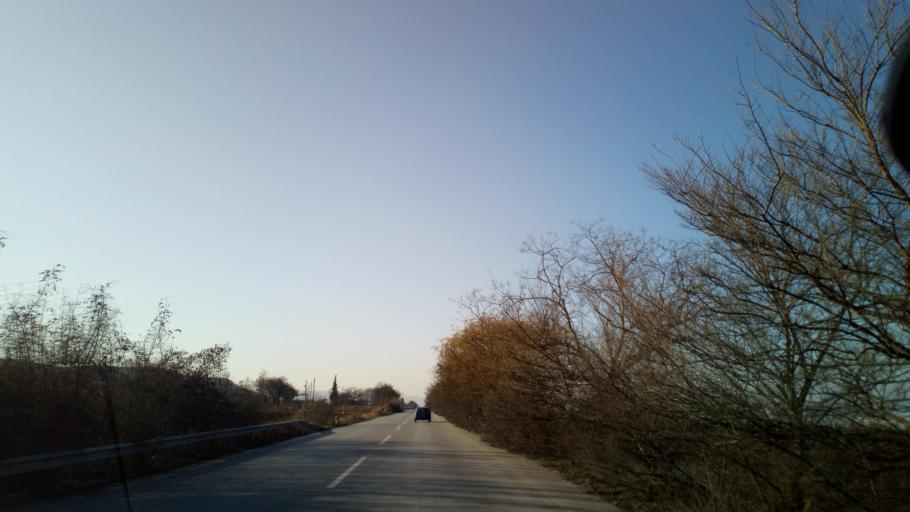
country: GR
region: Central Macedonia
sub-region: Nomos Thessalonikis
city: Gerakarou
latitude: 40.6499
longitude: 23.1710
